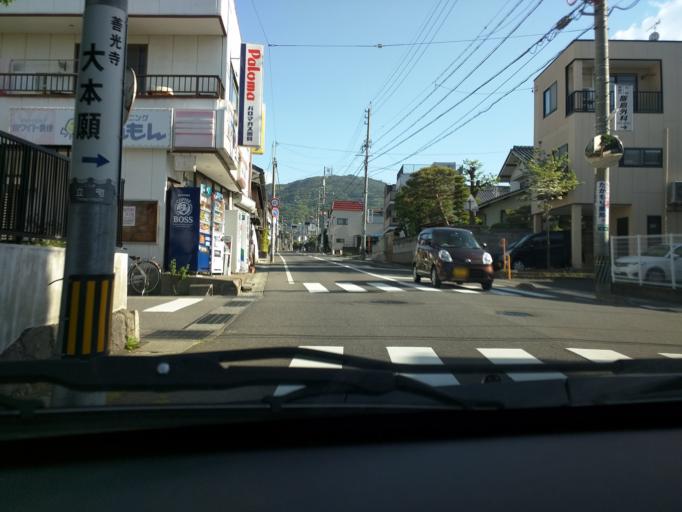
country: JP
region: Nagano
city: Nagano-shi
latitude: 36.6575
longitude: 138.1841
